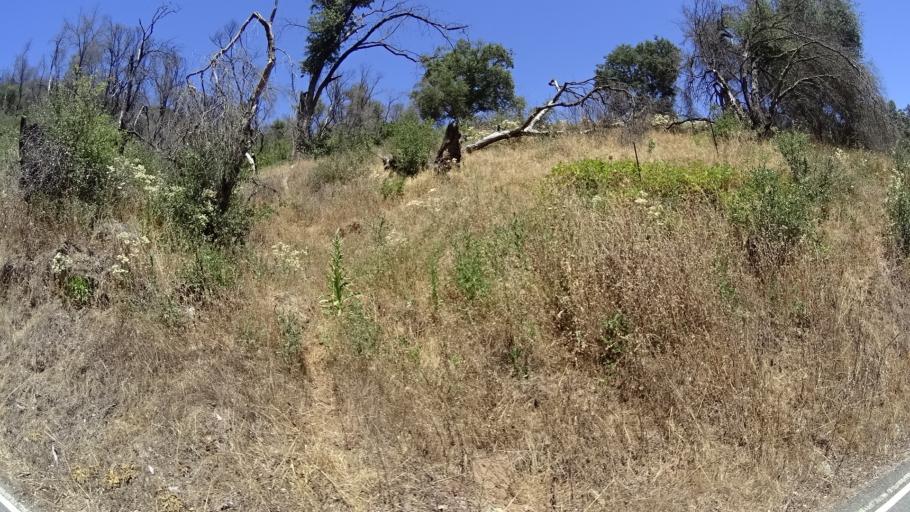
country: US
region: California
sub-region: Calaveras County
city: San Andreas
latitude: 38.2924
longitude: -120.6718
